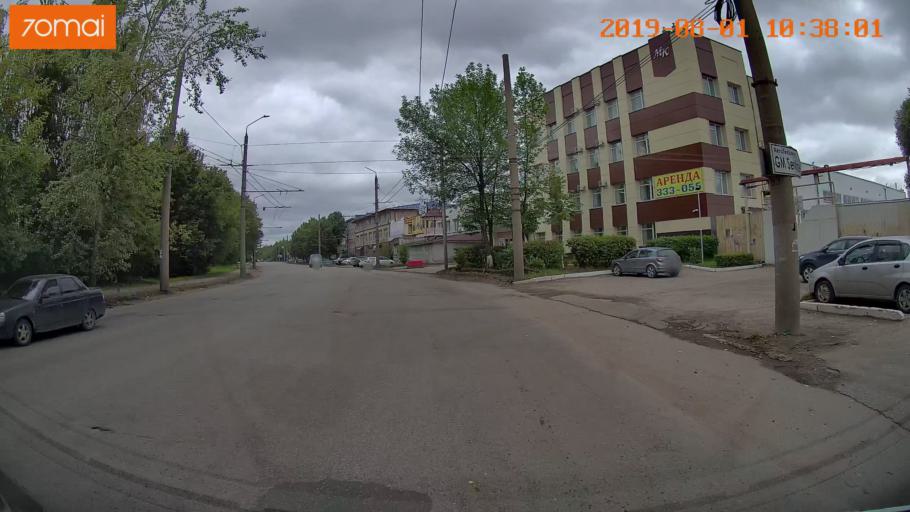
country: RU
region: Ivanovo
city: Kokhma
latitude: 56.9667
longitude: 41.0476
